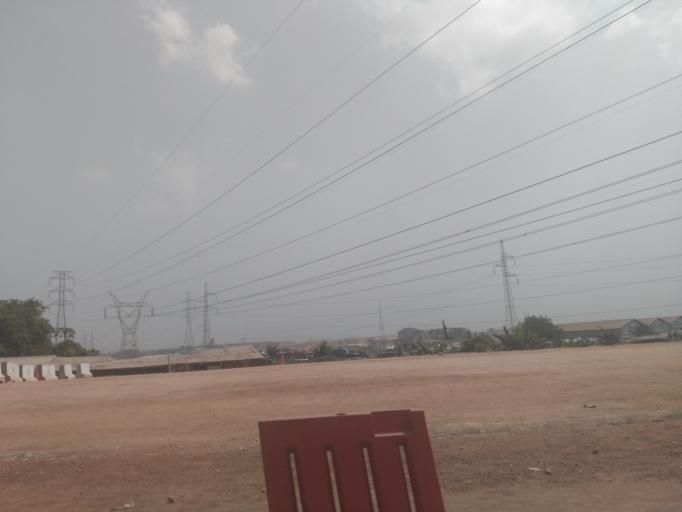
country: GH
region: Greater Accra
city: Tema
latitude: 5.6909
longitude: -0.0134
